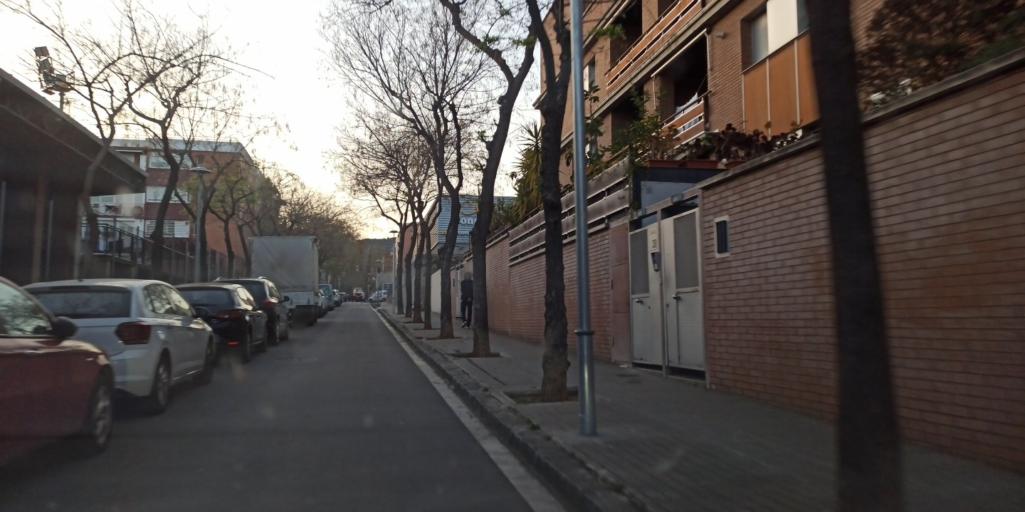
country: ES
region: Catalonia
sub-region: Provincia de Barcelona
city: Nou Barris
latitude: 41.4350
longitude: 2.1613
